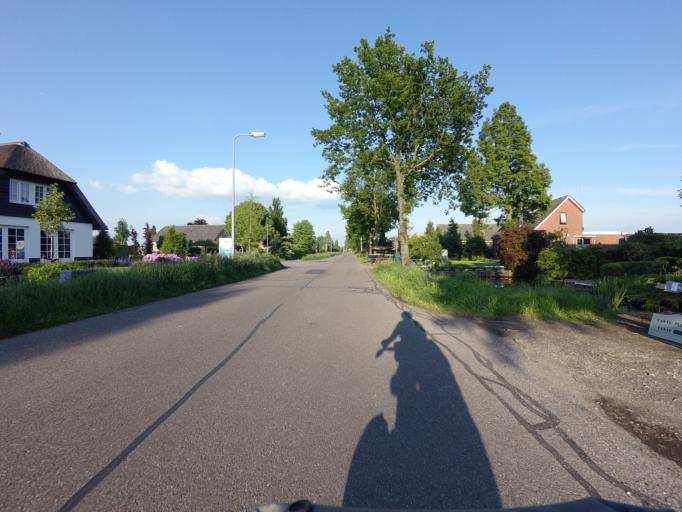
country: NL
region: South Holland
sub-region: Gemeente Boskoop
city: Boskoop
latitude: 52.0851
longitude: 4.6847
